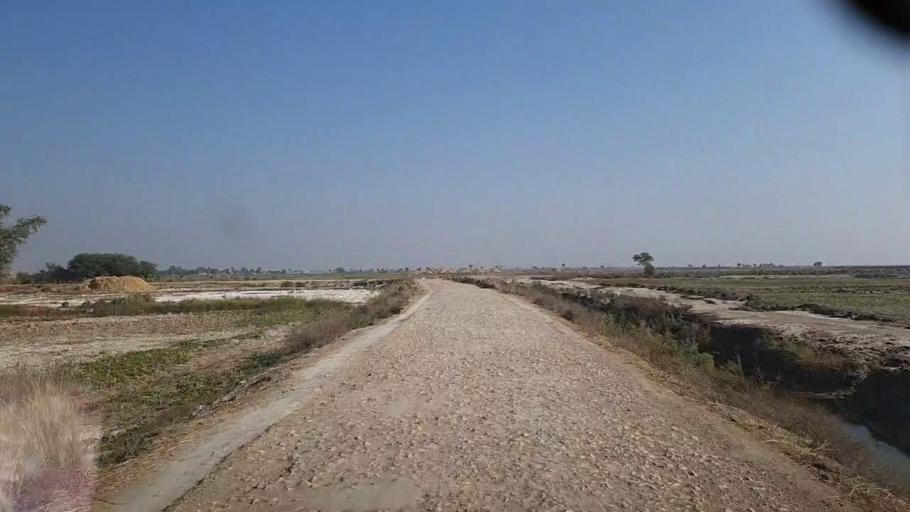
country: PK
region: Sindh
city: Jacobabad
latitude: 28.3059
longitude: 68.6067
